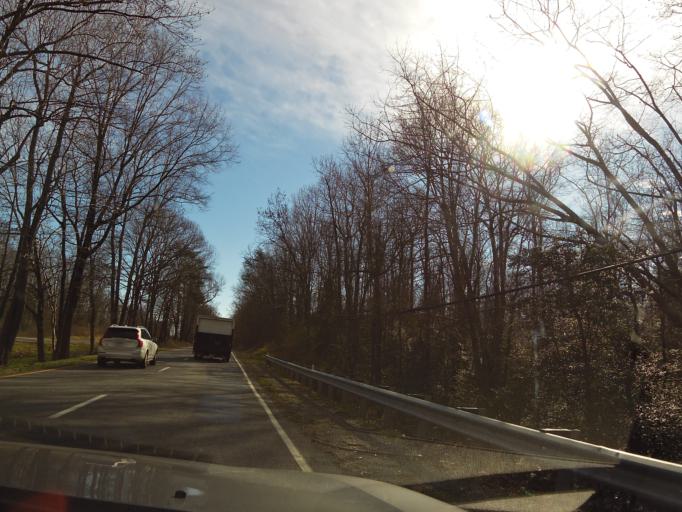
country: US
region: Virginia
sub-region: Chesterfield County
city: Enon
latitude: 37.3229
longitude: -77.3129
